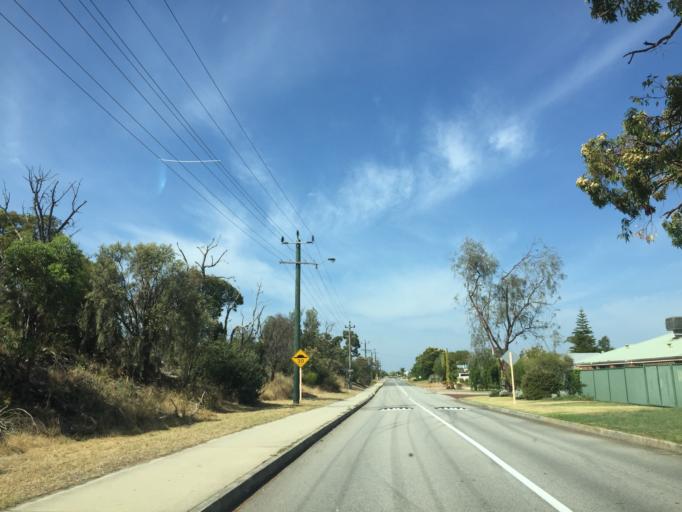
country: AU
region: Western Australia
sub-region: Gosnells
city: Thornlie
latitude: -32.0822
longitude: 115.9603
